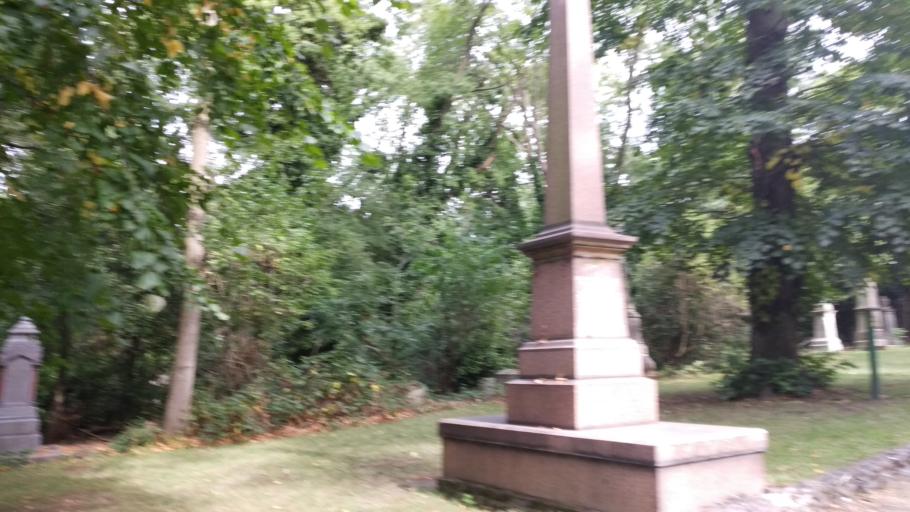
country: GB
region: England
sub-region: Greater London
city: Catford
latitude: 51.4636
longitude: -0.0519
